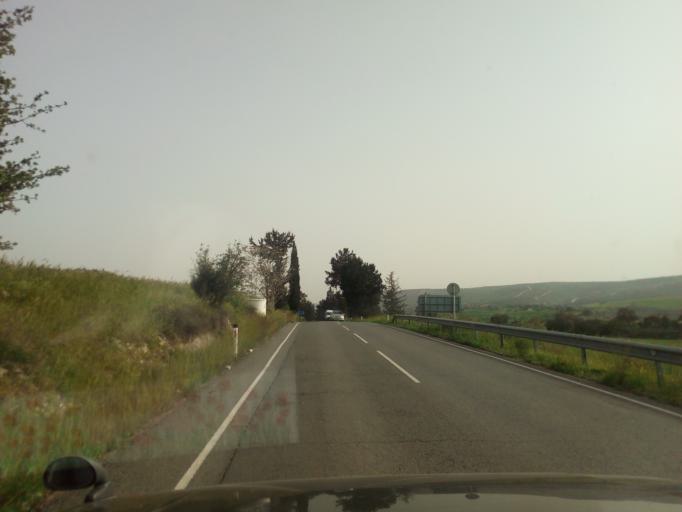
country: CY
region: Lefkosia
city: Lympia
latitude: 35.0035
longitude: 33.4990
